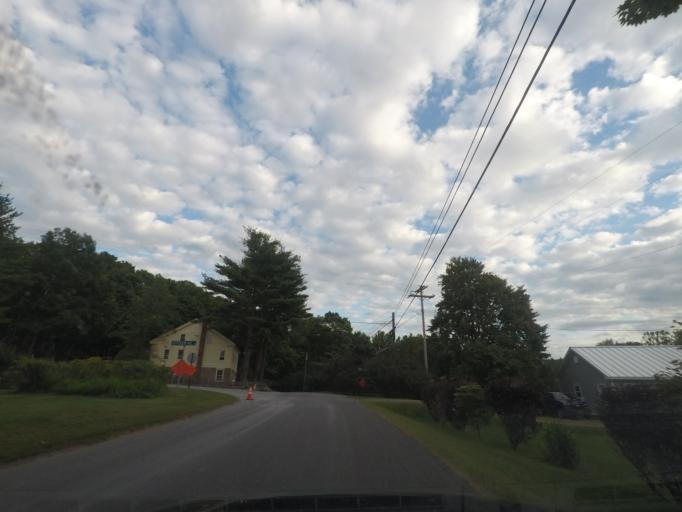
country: US
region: New York
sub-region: Rensselaer County
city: Nassau
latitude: 42.4850
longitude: -73.5957
